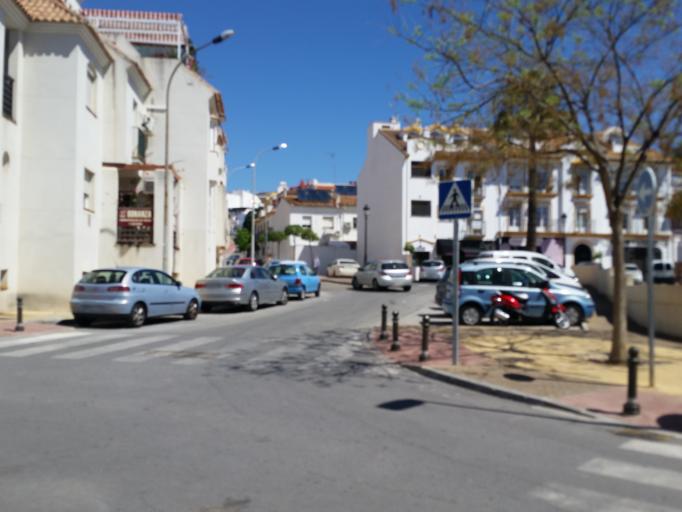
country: ES
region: Andalusia
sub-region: Provincia de Malaga
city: Benalmadena
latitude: 36.6000
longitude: -4.5367
